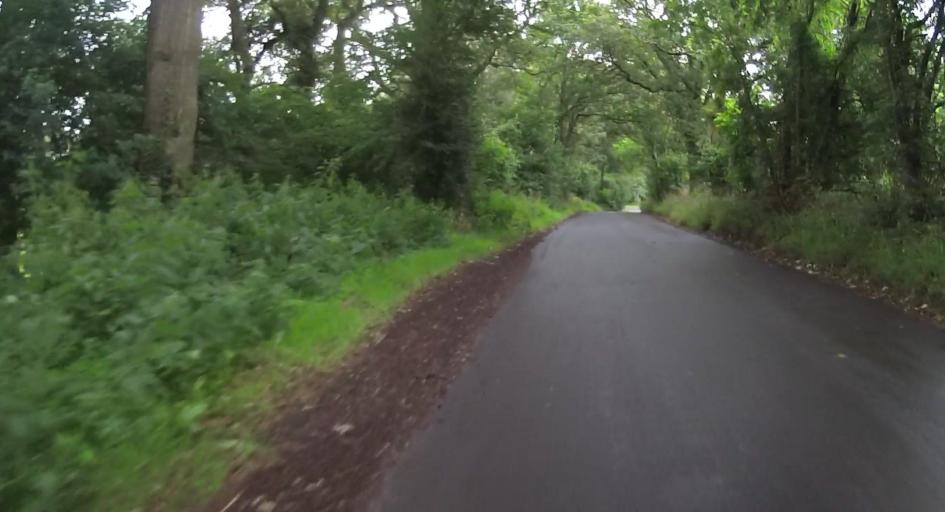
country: GB
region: England
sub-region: Hampshire
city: Andover
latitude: 51.1995
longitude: -1.4088
